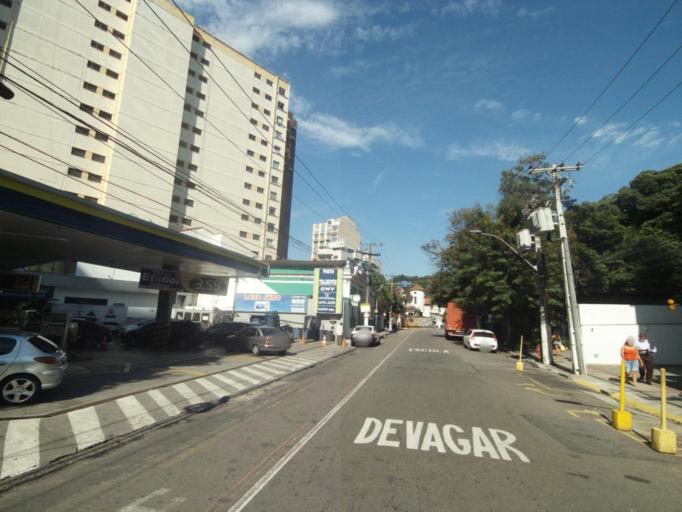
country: BR
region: Rio de Janeiro
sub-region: Niteroi
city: Niteroi
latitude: -22.9016
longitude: -43.1255
